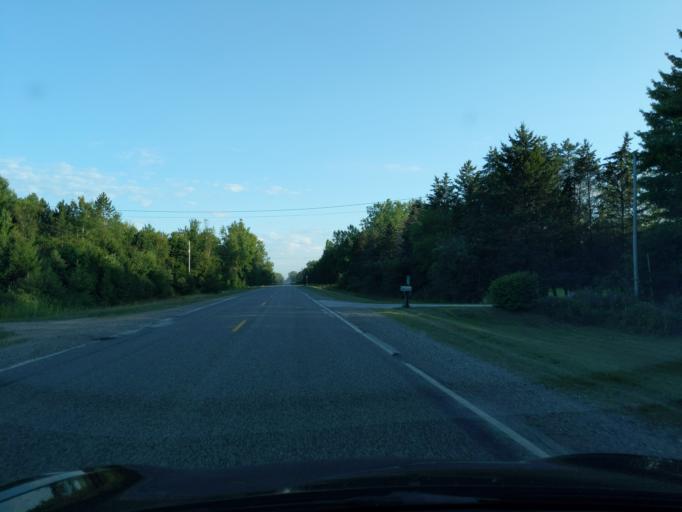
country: US
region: Michigan
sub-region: Gratiot County
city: Breckenridge
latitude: 43.4568
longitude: -84.3699
